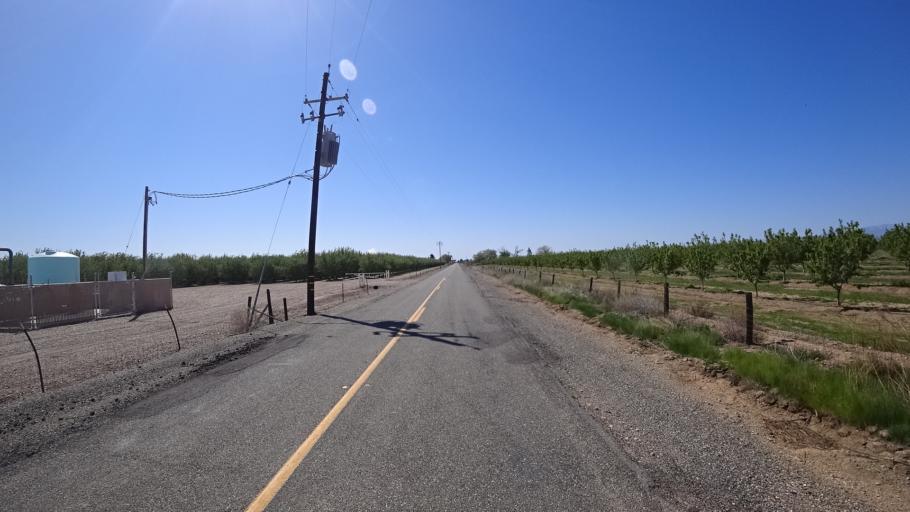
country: US
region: California
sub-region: Glenn County
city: Orland
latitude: 39.6443
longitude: -122.2533
